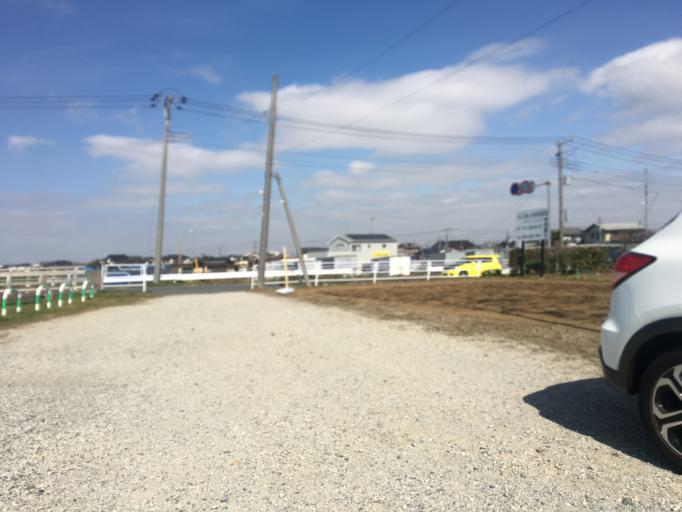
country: JP
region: Saitama
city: Shiki
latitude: 35.8604
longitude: 139.5572
